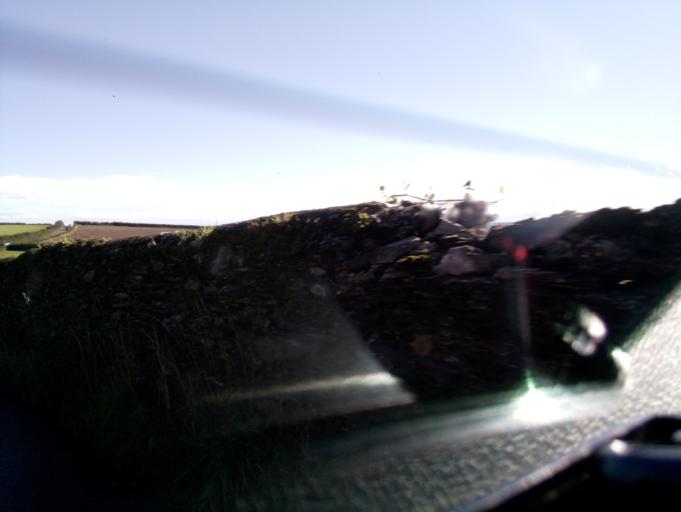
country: GB
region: England
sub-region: Devon
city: Dartmouth
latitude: 50.3433
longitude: -3.5905
